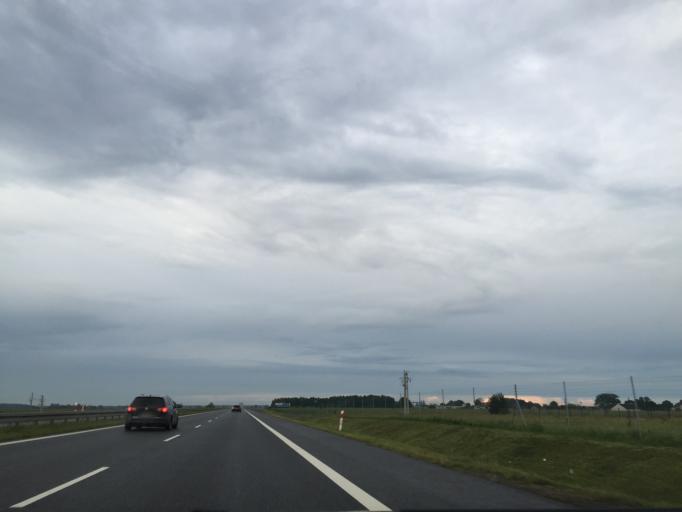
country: PL
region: Podlasie
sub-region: Powiat zambrowski
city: Zambrow
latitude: 53.0014
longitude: 22.2594
